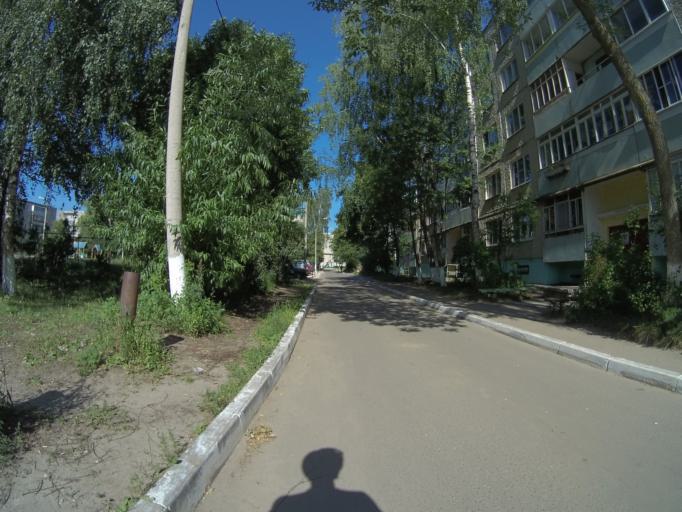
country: RU
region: Vladimir
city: Vorsha
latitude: 56.0983
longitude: 40.1981
